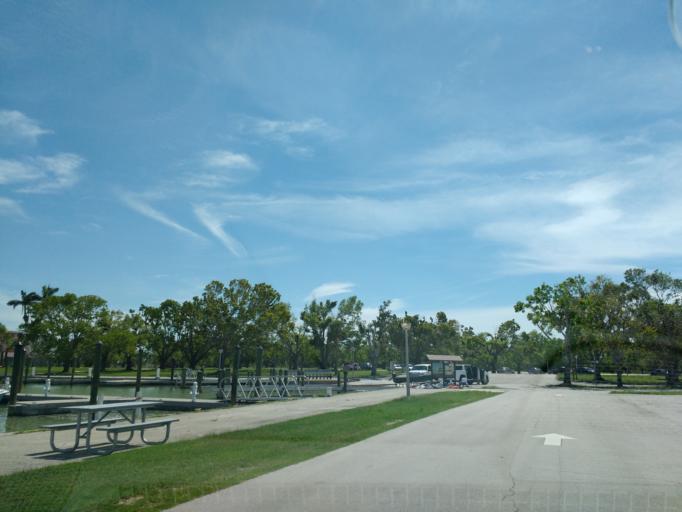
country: US
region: Florida
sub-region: Monroe County
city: Islamorada
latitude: 25.1426
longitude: -80.9230
